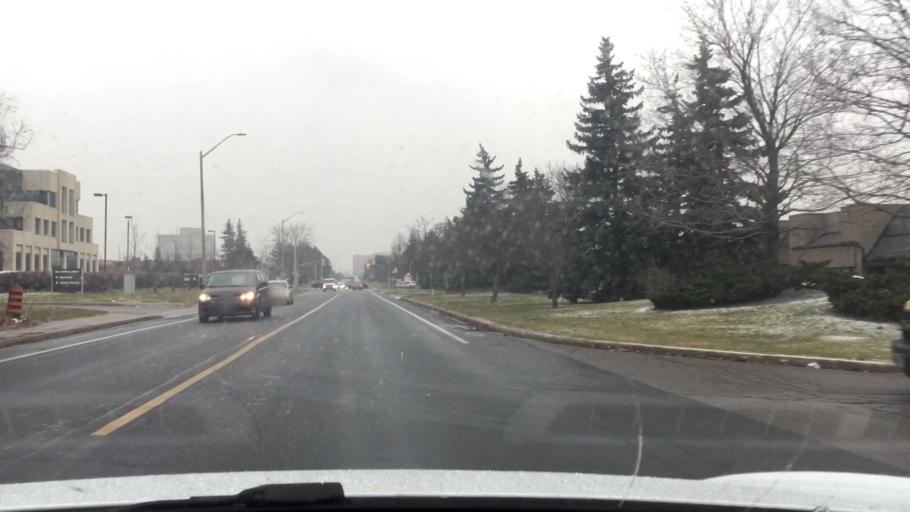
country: CA
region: Ontario
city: Markham
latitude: 43.8288
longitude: -79.3286
